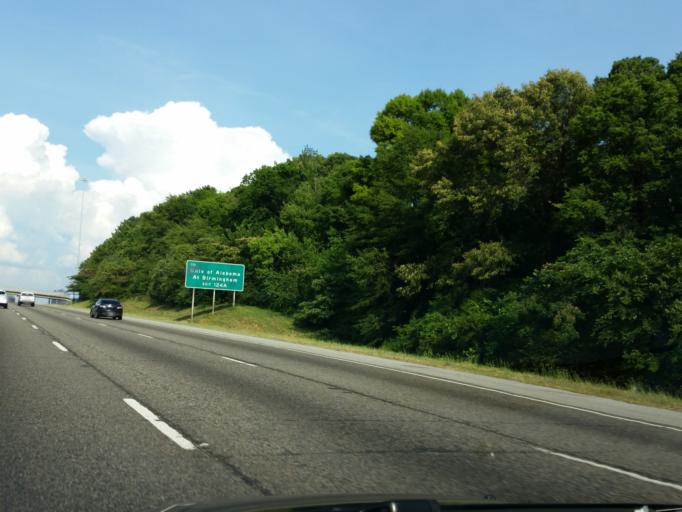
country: US
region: Alabama
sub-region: Jefferson County
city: Birmingham
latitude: 33.5208
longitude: -86.8409
